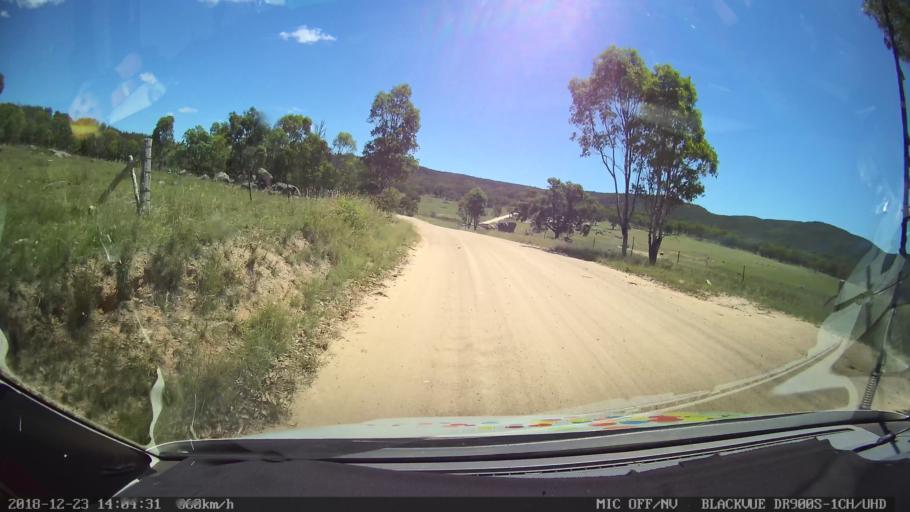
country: AU
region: New South Wales
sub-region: Tamworth Municipality
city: Manilla
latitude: -30.6225
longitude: 151.0894
